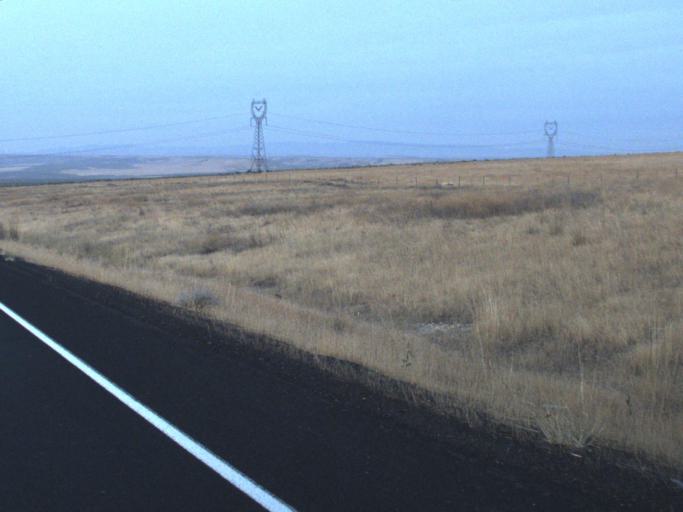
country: US
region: Washington
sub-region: Yakima County
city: Toppenish
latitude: 46.2690
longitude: -120.4027
